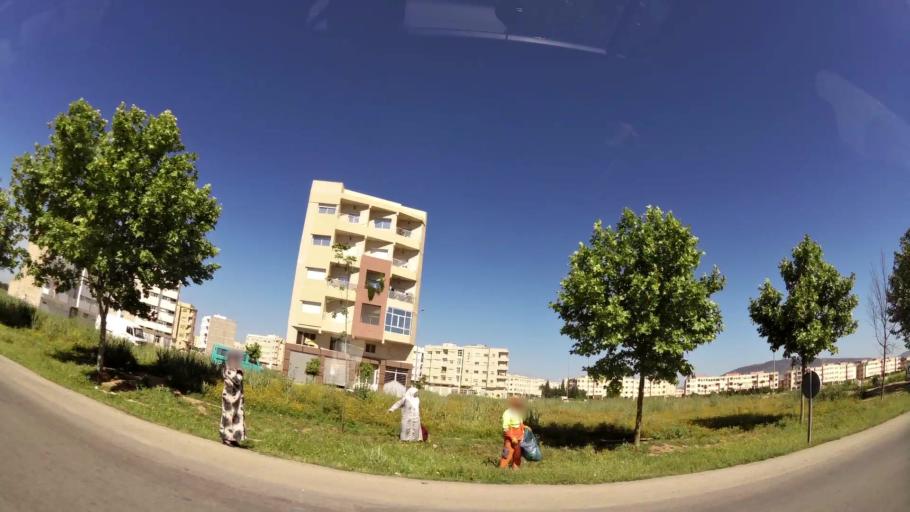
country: MA
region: Fes-Boulemane
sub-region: Fes
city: Fes
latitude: 34.0106
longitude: -5.0209
